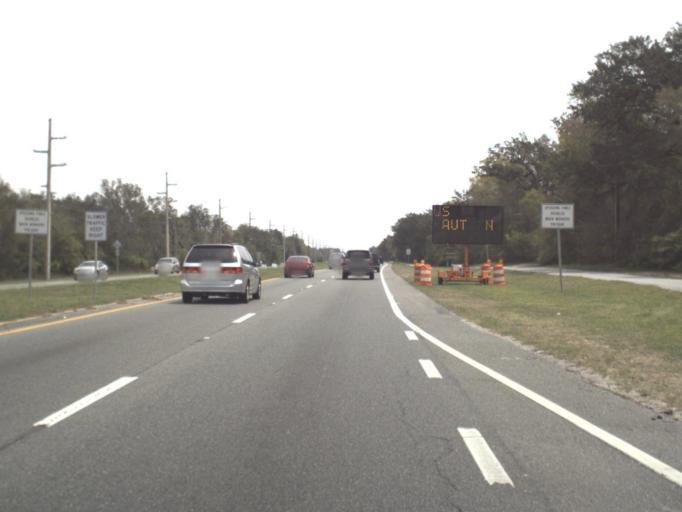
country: US
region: Florida
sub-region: Santa Rosa County
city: Gulf Breeze
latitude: 30.3590
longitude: -87.1546
